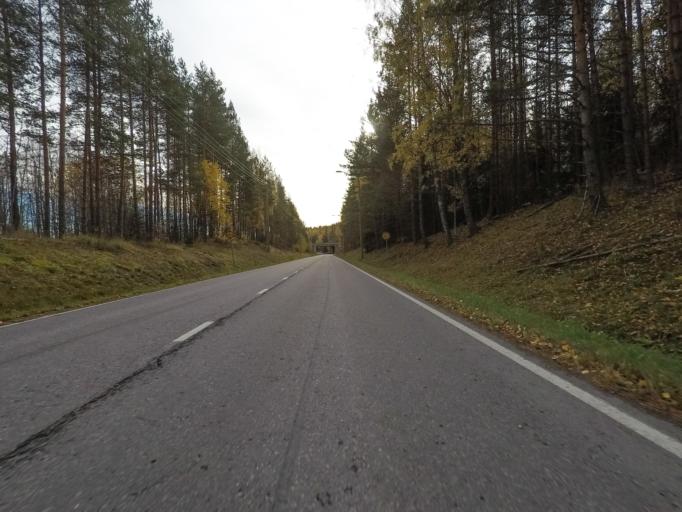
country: FI
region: Uusimaa
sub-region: Helsinki
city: Vantaa
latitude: 60.2624
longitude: 25.1411
